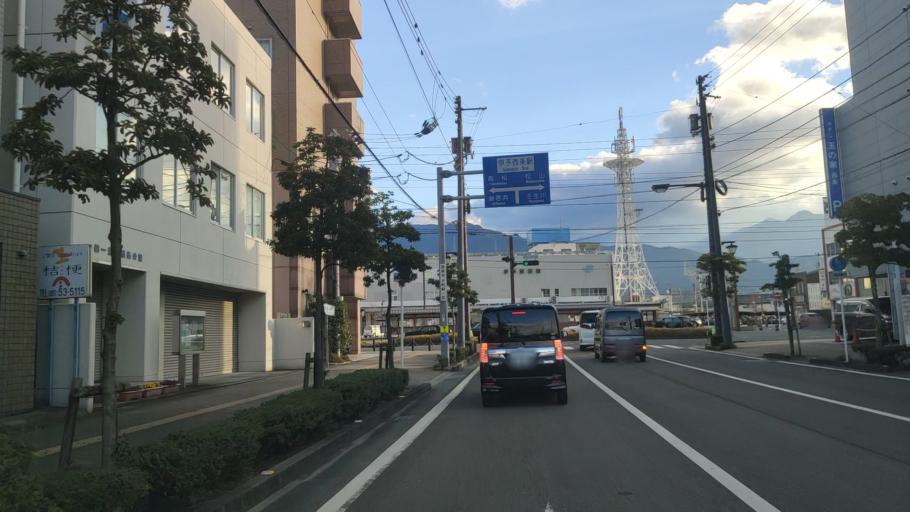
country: JP
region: Ehime
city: Saijo
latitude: 33.9134
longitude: 133.1871
